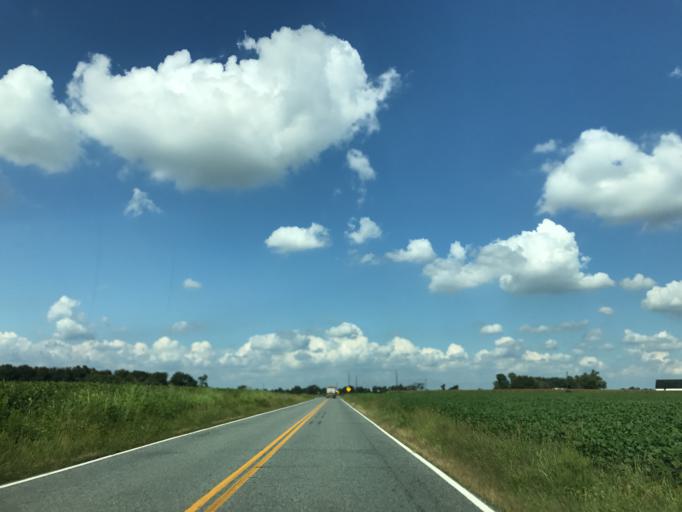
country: US
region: Delaware
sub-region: New Castle County
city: Middletown
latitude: 39.3874
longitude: -75.8001
